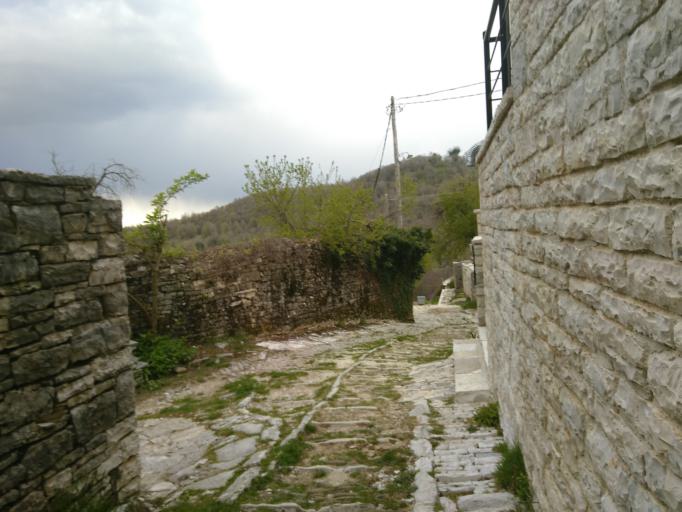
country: GR
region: Epirus
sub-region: Nomos Ioanninon
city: Asprangeloi
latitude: 39.8818
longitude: 20.7469
